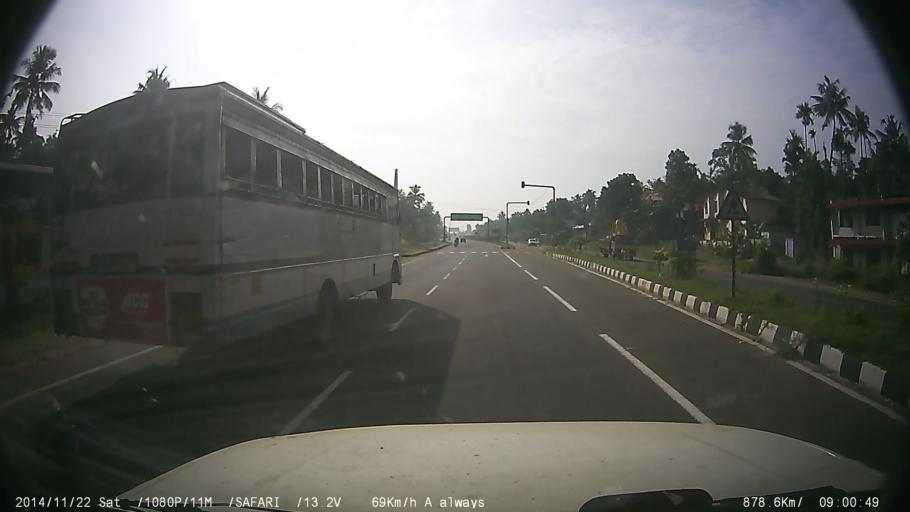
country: IN
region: Kerala
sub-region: Thrissur District
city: Kizhake Chalakudi
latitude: 10.3797
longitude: 76.2983
